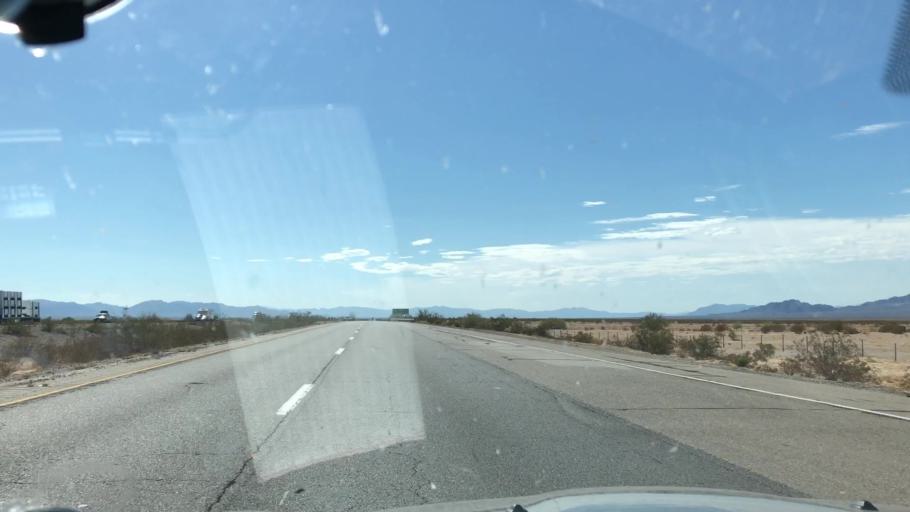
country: US
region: California
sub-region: Riverside County
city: Mesa Verde
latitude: 33.6086
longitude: -114.9935
